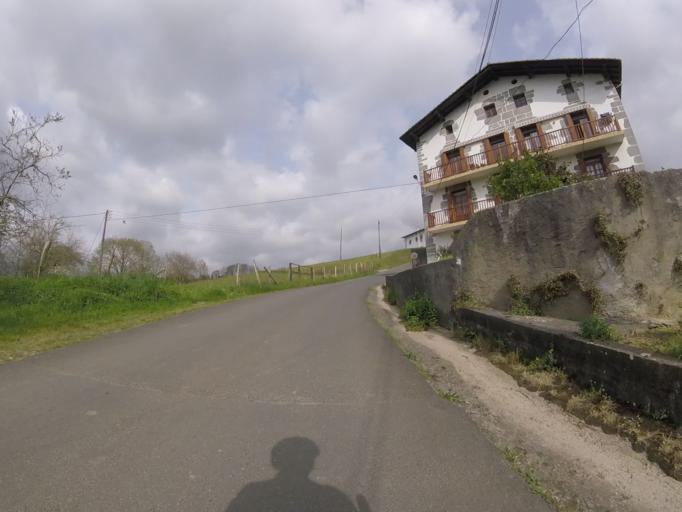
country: ES
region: Basque Country
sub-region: Provincia de Guipuzcoa
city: Zizurkil
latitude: 43.1999
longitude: -2.0747
